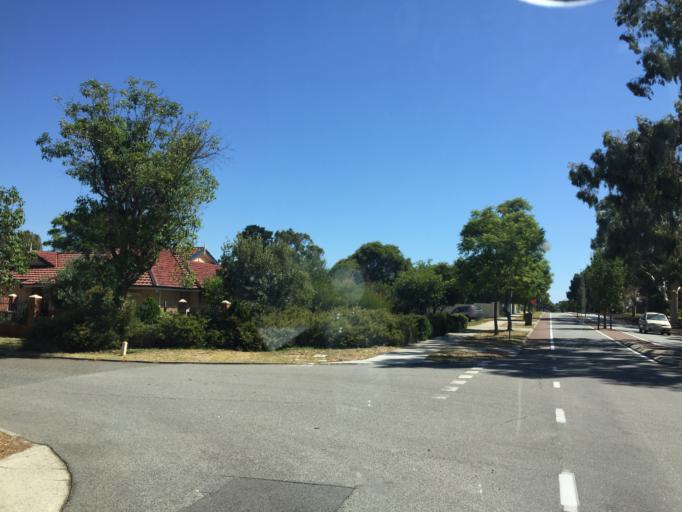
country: AU
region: Western Australia
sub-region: Victoria Park
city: Victoria Park
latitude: -31.9729
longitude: 115.9105
